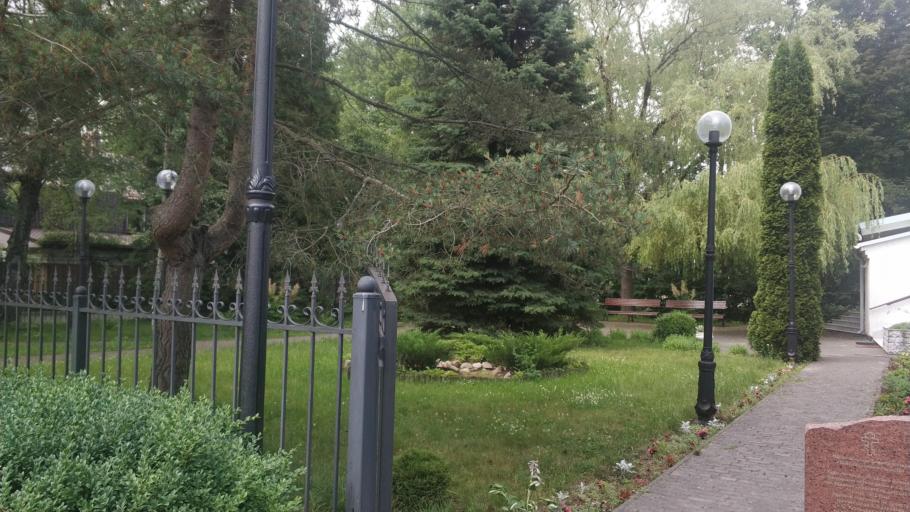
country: RU
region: Kaliningrad
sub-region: Gorod Svetlogorsk
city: Svetlogorsk
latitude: 54.9437
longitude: 20.1623
